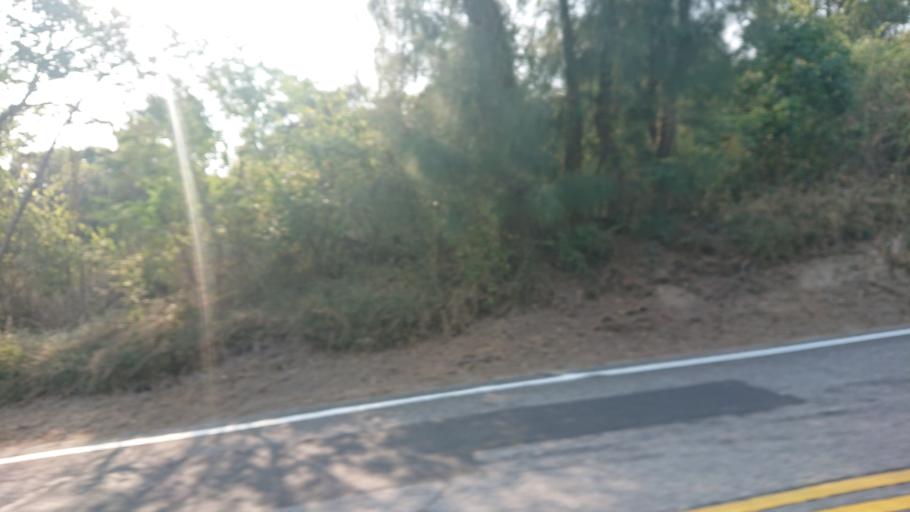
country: CN
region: Fujian
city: Shijing
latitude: 24.4995
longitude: 118.4436
